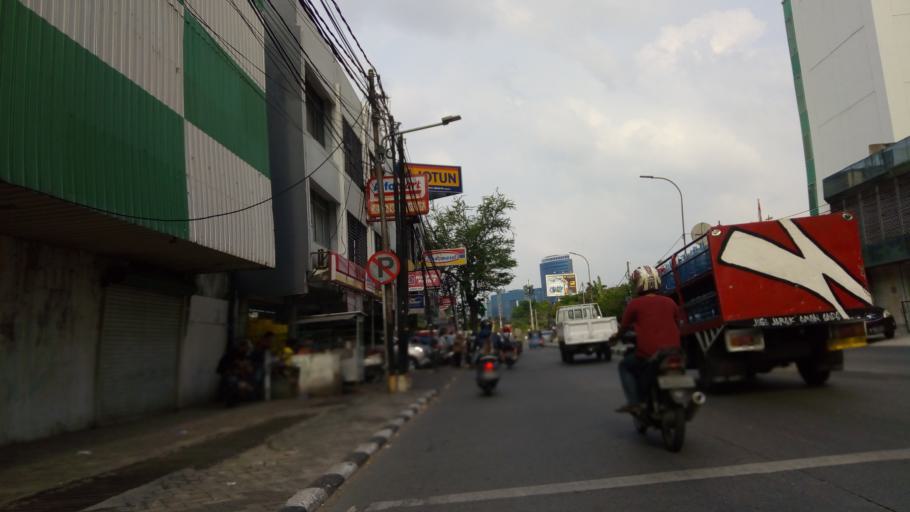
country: ID
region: Jakarta Raya
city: Jakarta
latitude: -6.1472
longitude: 106.8364
